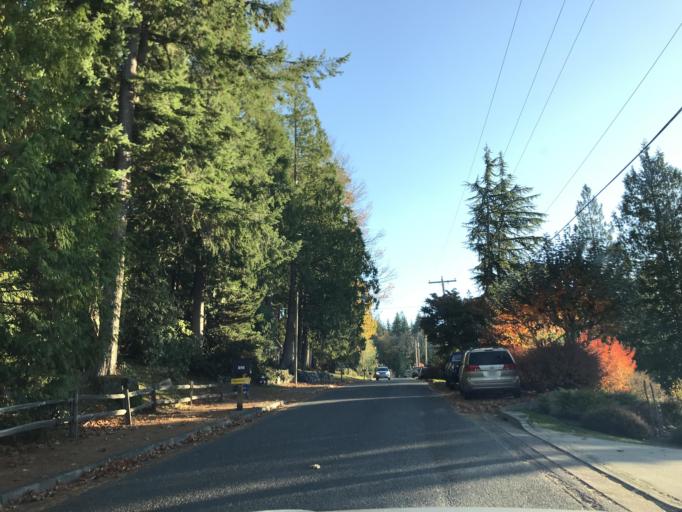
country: US
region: Washington
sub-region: Whatcom County
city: Geneva
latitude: 48.7472
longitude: -122.4264
